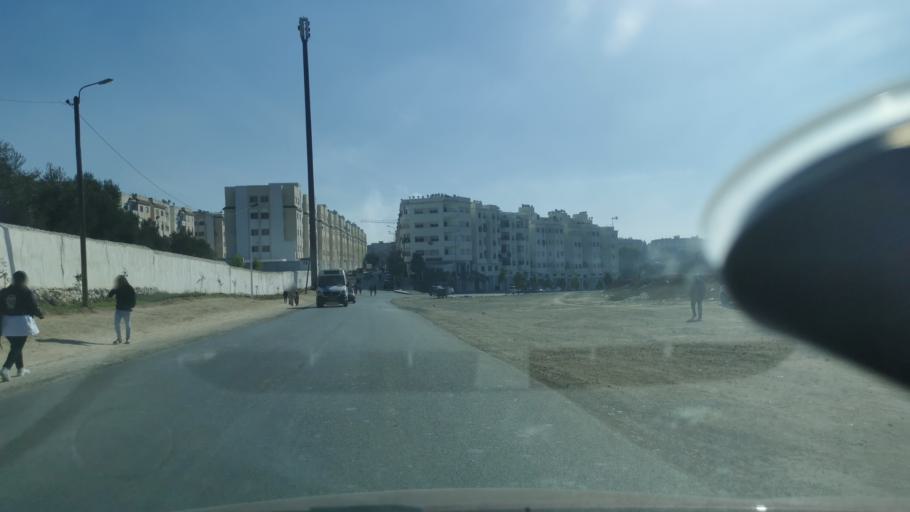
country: MA
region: Fes-Boulemane
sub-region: Fes
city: Fes
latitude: 34.0396
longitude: -4.9895
